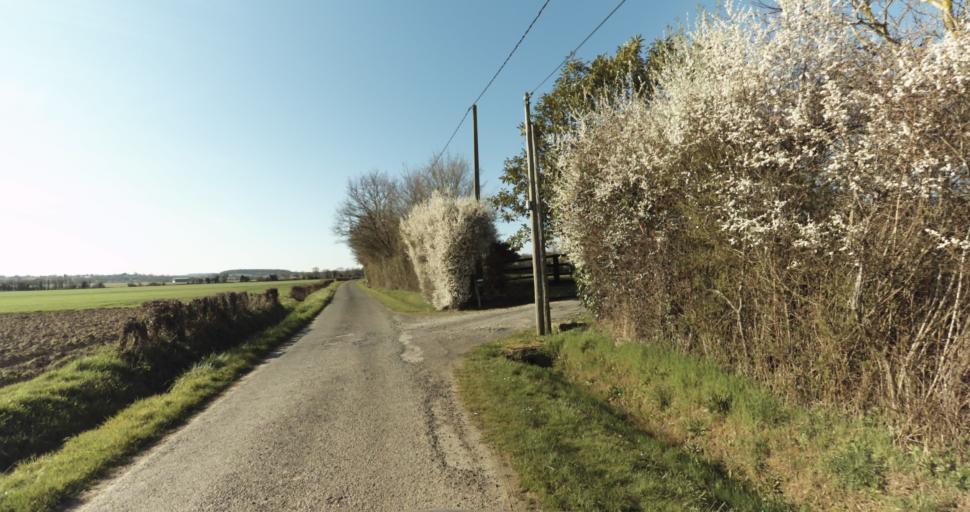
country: FR
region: Lower Normandy
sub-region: Departement du Calvados
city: Saint-Pierre-sur-Dives
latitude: 49.0485
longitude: 0.0237
